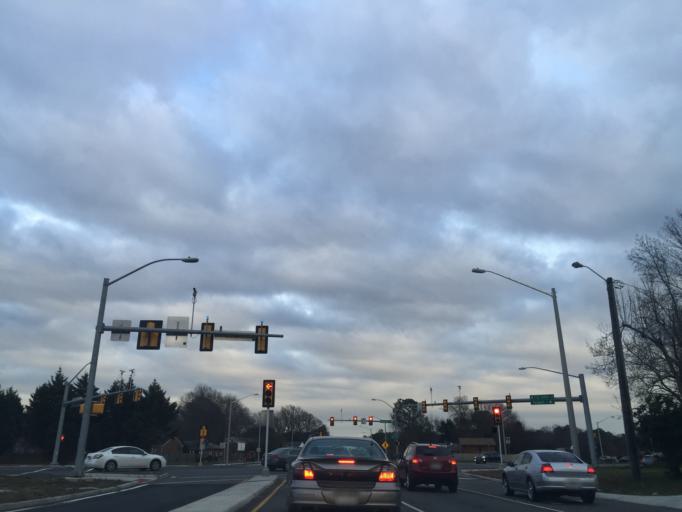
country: US
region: Virginia
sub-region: City of Newport News
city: Newport News
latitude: 37.0877
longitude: -76.5012
